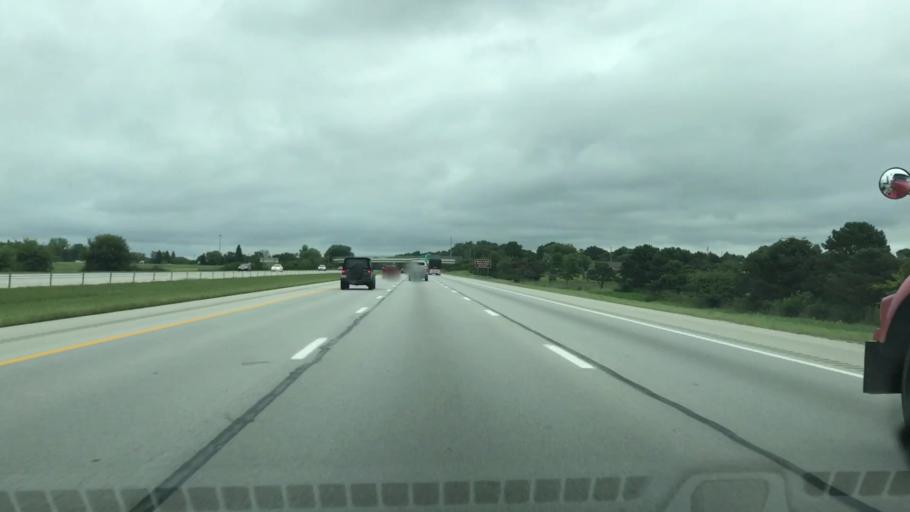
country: US
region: Ohio
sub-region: Clark County
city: Lisbon
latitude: 39.9135
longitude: -83.7005
